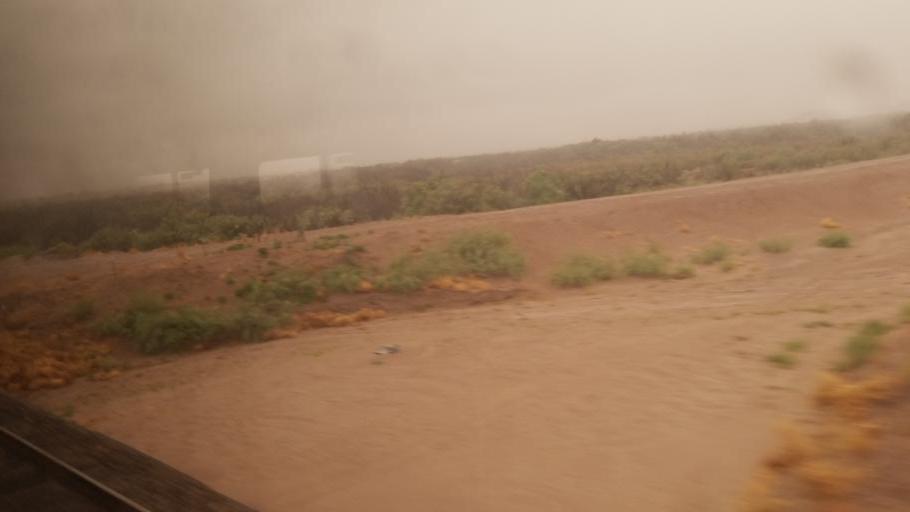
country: US
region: Arizona
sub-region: Navajo County
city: Joseph City
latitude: 34.9501
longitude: -110.3383
